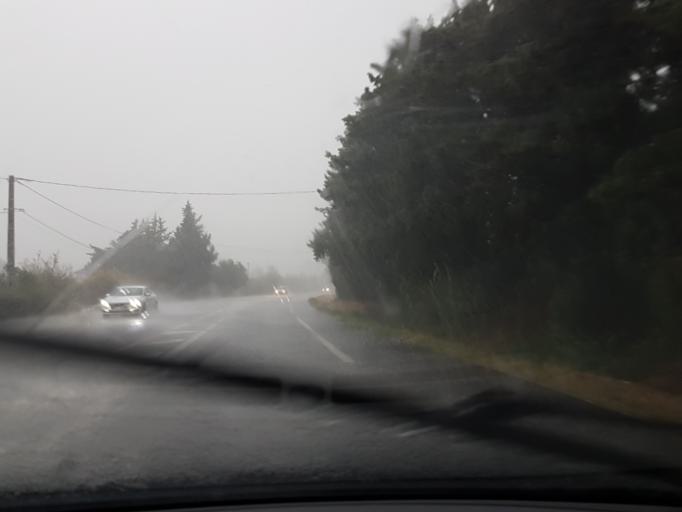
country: FR
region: Provence-Alpes-Cote d'Azur
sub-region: Departement du Vaucluse
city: Pernes-les-Fontaines
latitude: 44.0182
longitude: 5.0320
